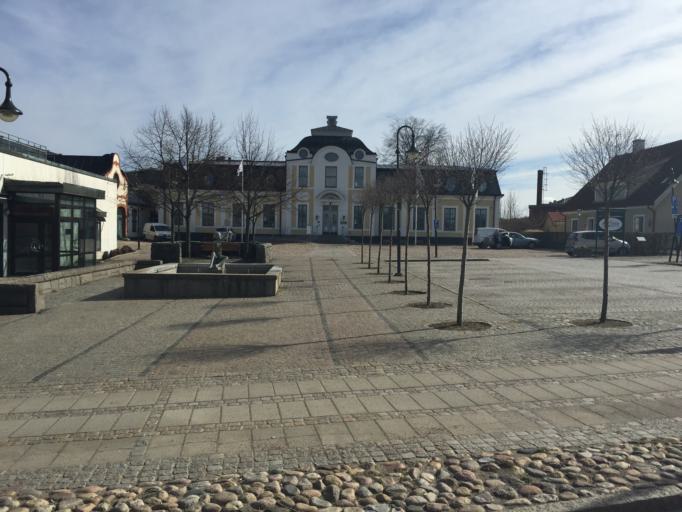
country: SE
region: Skane
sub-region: Sjobo Kommun
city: Sjoebo
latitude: 55.6317
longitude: 13.7062
